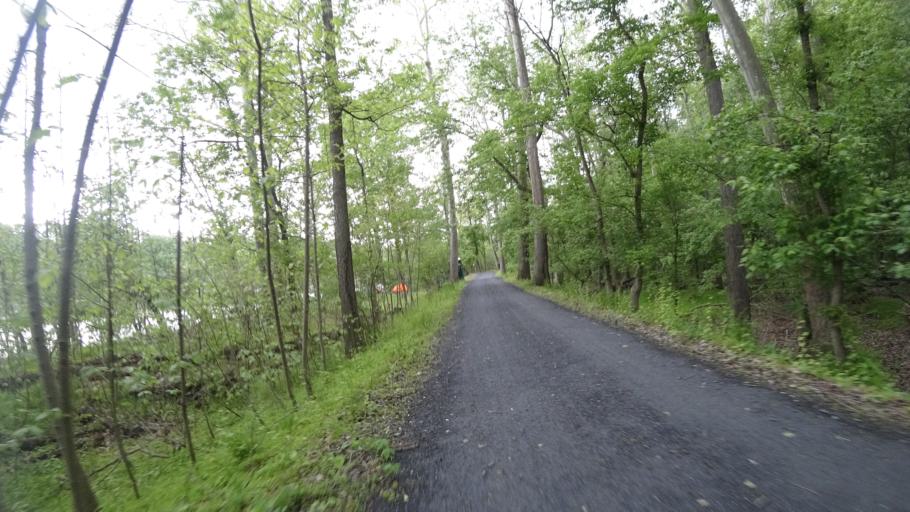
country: US
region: West Virginia
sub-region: Jefferson County
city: Bolivar
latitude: 39.3409
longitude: -77.7574
